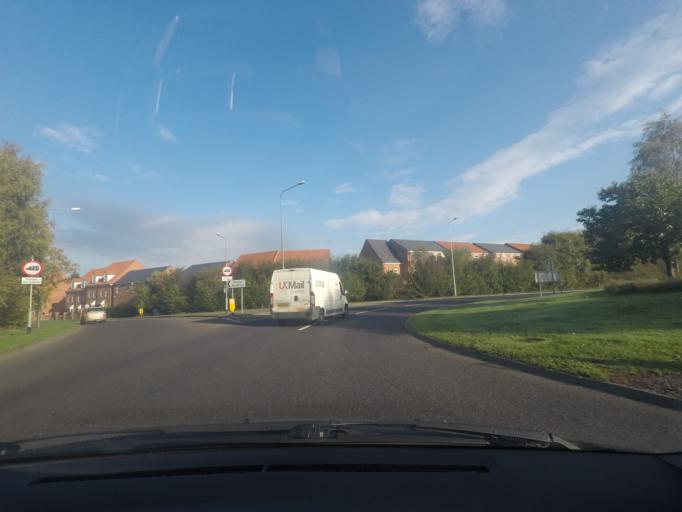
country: GB
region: England
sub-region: East Riding of Yorkshire
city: Market Weighton
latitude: 53.8588
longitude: -0.6570
